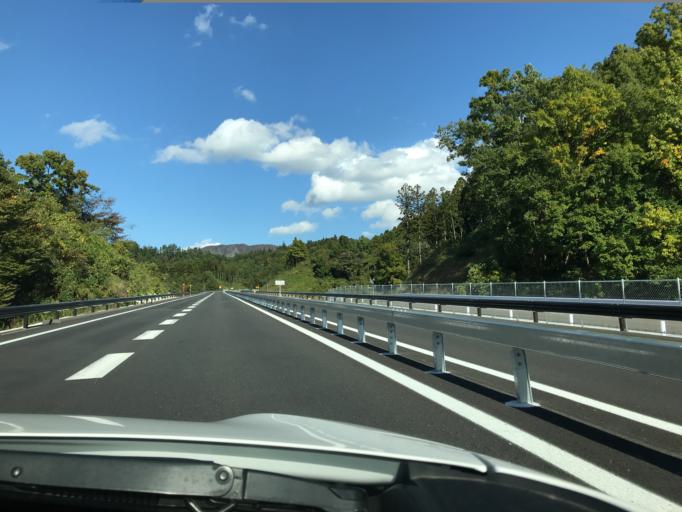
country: JP
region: Fukushima
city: Yanagawamachi-saiwaicho
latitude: 37.7504
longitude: 140.6457
